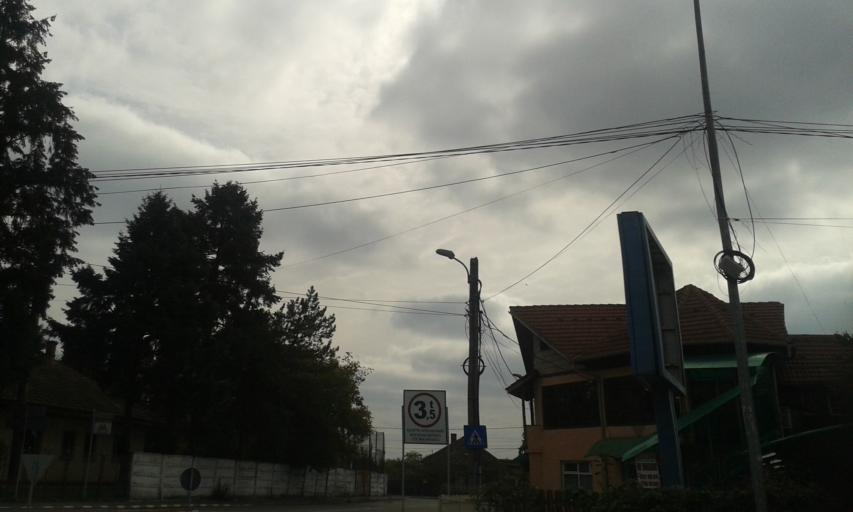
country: RO
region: Gorj
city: Targu Jiu
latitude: 45.0369
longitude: 23.2895
